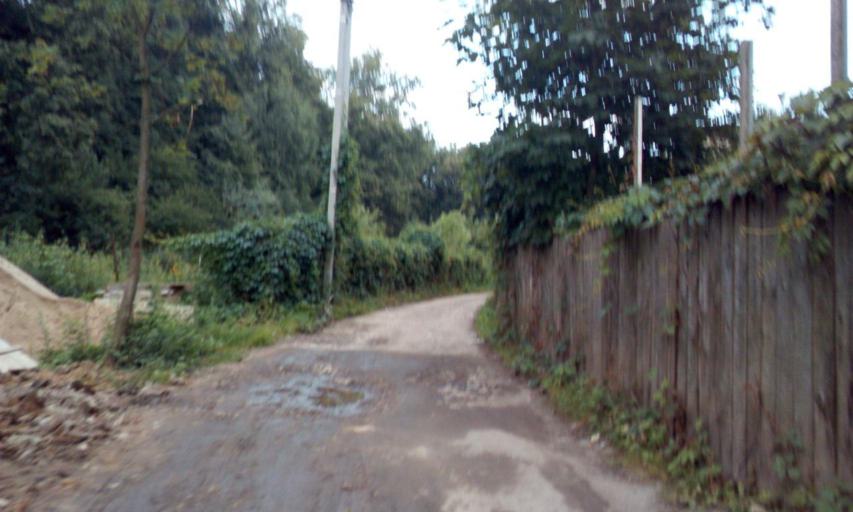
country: RU
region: Moskovskaya
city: Moskovskiy
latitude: 55.6060
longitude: 37.3262
